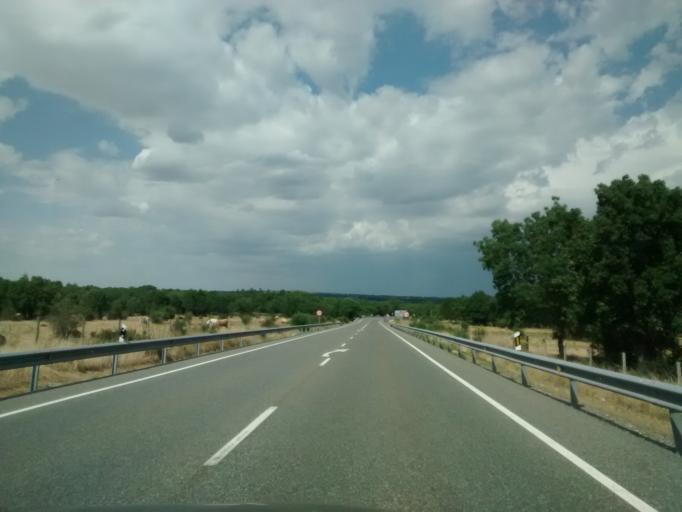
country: ES
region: Castille and Leon
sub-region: Provincia de Segovia
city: Gallegos
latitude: 41.0863
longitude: -3.7915
